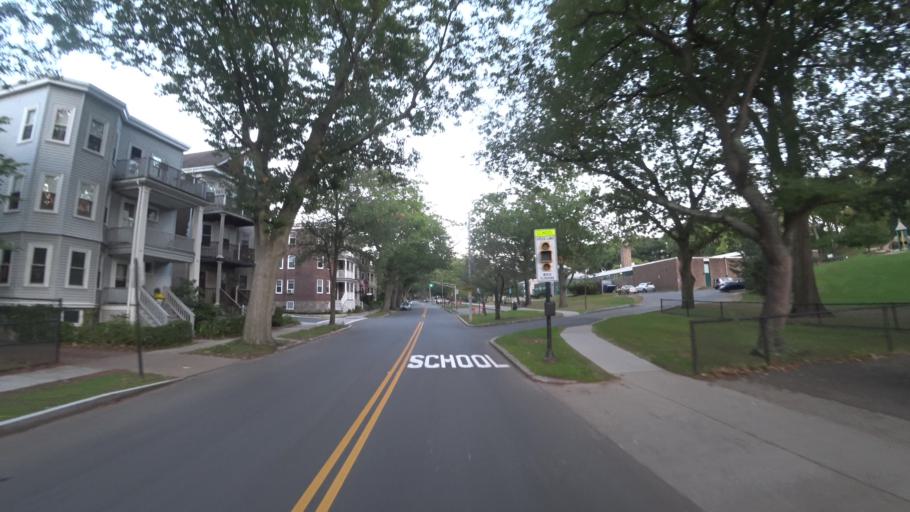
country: US
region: Massachusetts
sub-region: Norfolk County
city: Brookline
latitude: 42.3288
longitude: -71.1490
